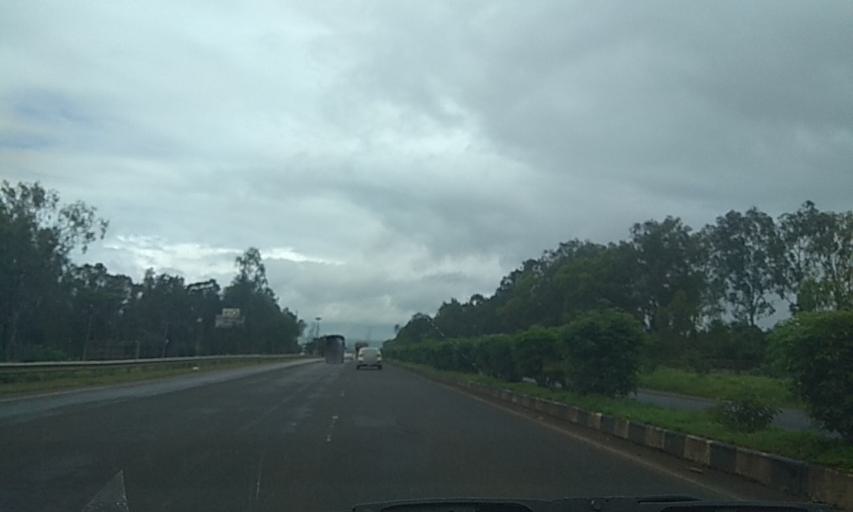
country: IN
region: Karnataka
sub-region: Belgaum
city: Belgaum
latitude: 15.8905
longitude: 74.5241
